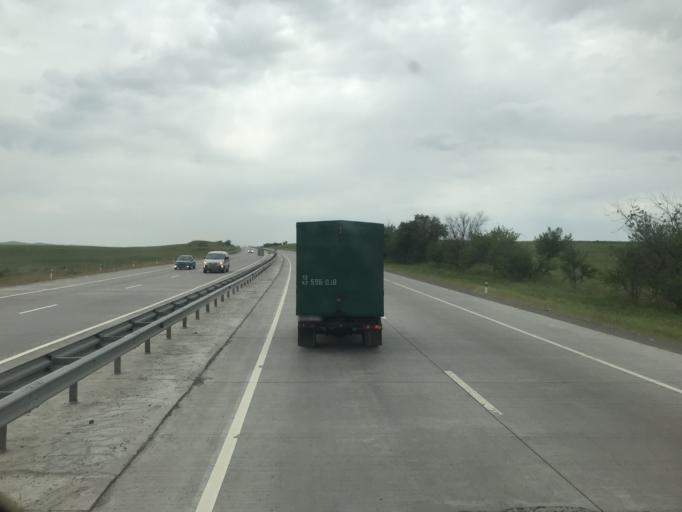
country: KZ
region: Ongtustik Qazaqstan
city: Shymkent
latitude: 42.2032
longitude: 69.5108
